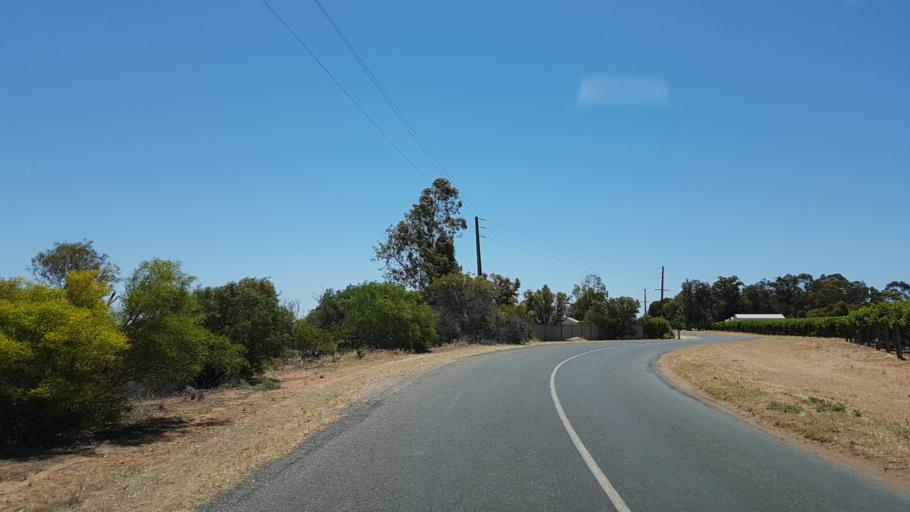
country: AU
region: South Australia
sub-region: Loxton Waikerie
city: Waikerie
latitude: -34.1730
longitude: 140.0307
